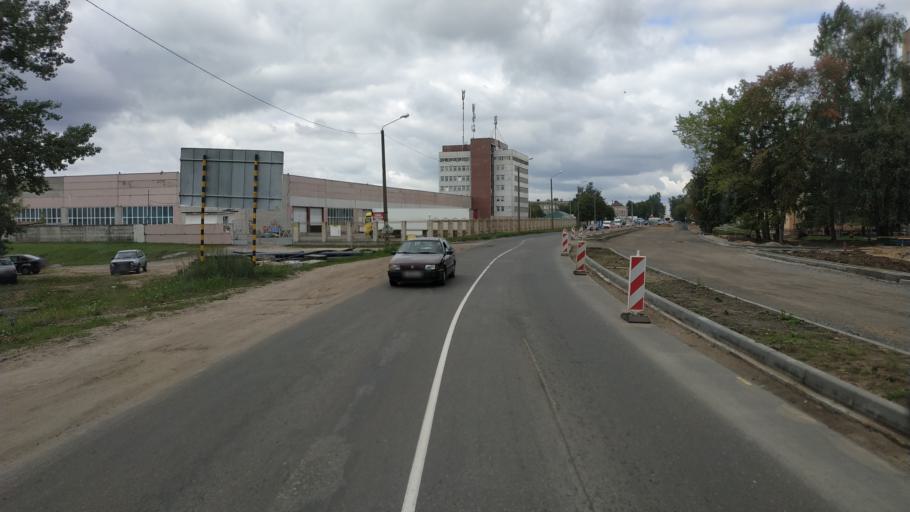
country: BY
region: Mogilev
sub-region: Mahilyowski Rayon
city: Veyno
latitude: 53.8804
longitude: 30.4088
